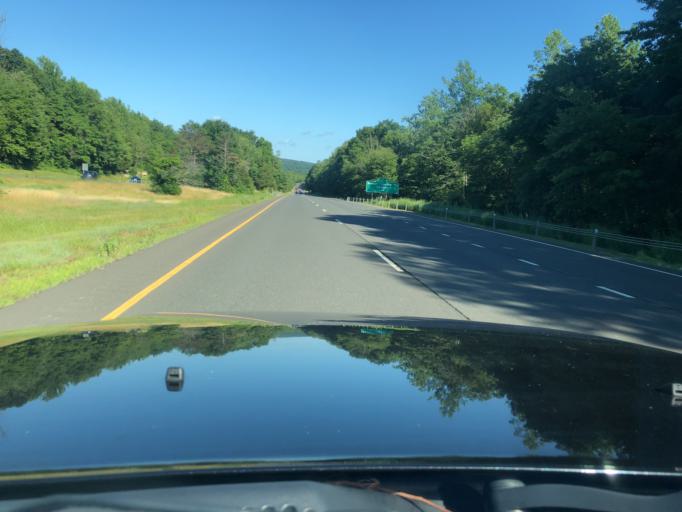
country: US
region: Connecticut
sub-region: Middlesex County
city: Higganum
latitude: 41.4666
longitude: -72.5468
